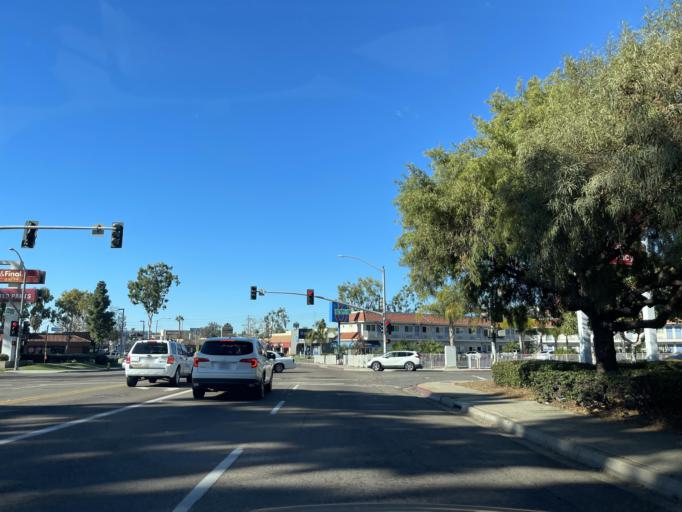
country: US
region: California
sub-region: San Diego County
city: National City
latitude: 32.6772
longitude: -117.0937
